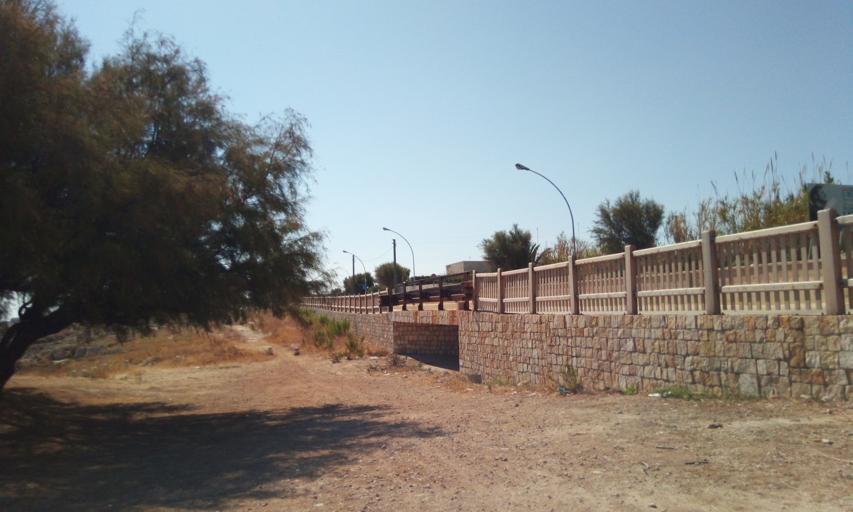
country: IT
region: Apulia
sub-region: Provincia di Bari
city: Polignano a Mare
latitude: 41.0019
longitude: 17.2046
